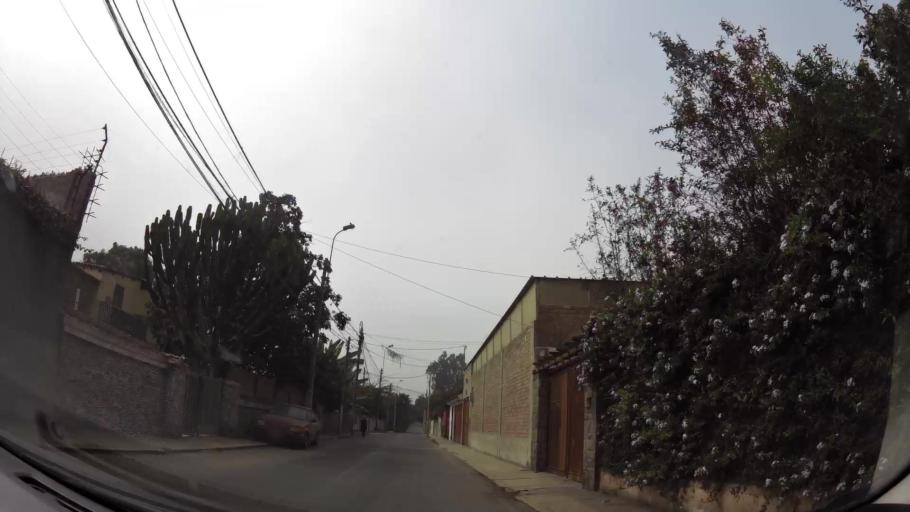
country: PE
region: Lima
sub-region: Lima
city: Chaclacayo
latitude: -11.9799
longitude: -76.7747
